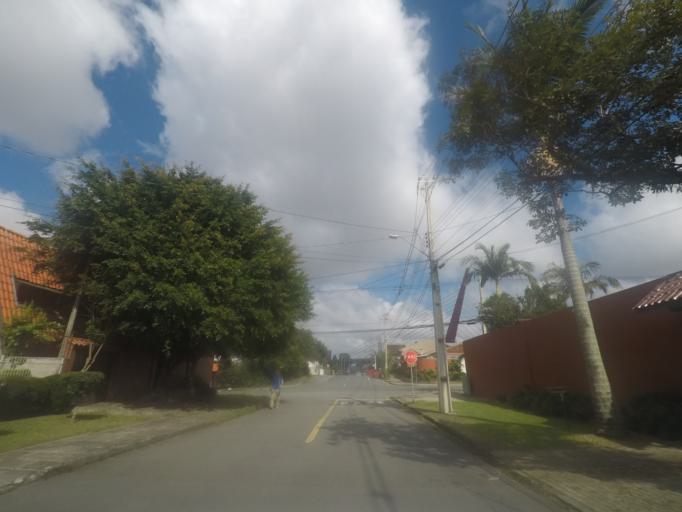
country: BR
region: Parana
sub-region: Pinhais
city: Pinhais
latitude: -25.4638
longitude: -49.2320
